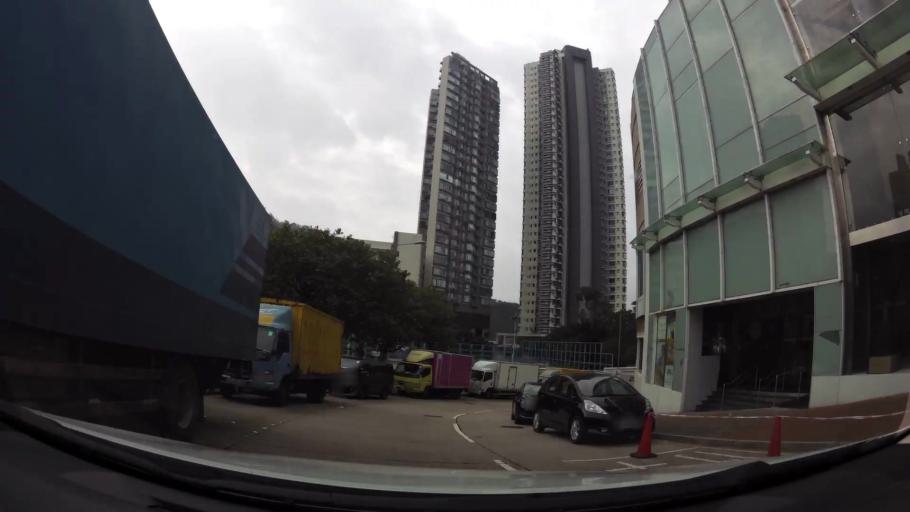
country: HK
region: Kowloon City
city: Kowloon
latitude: 22.2940
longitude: 114.2370
